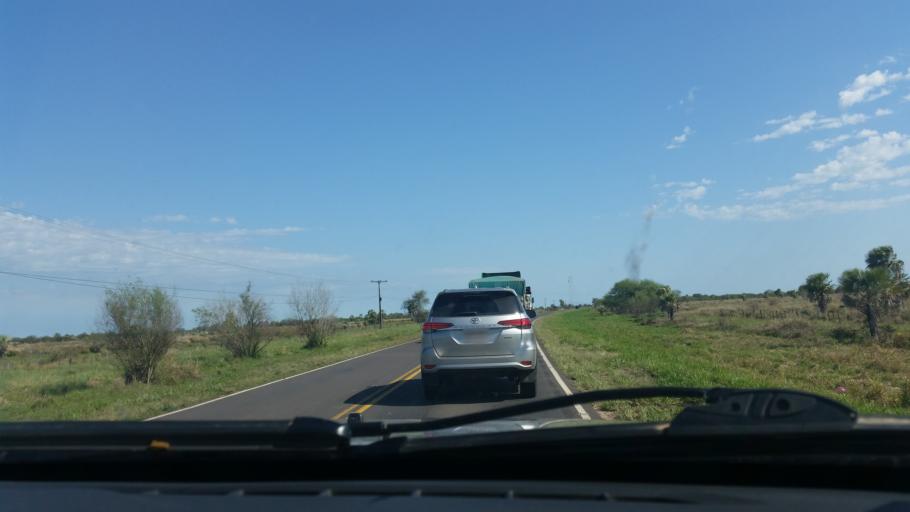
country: PY
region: Presidente Hayes
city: Benjamin Aceval
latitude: -24.6733
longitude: -57.9852
